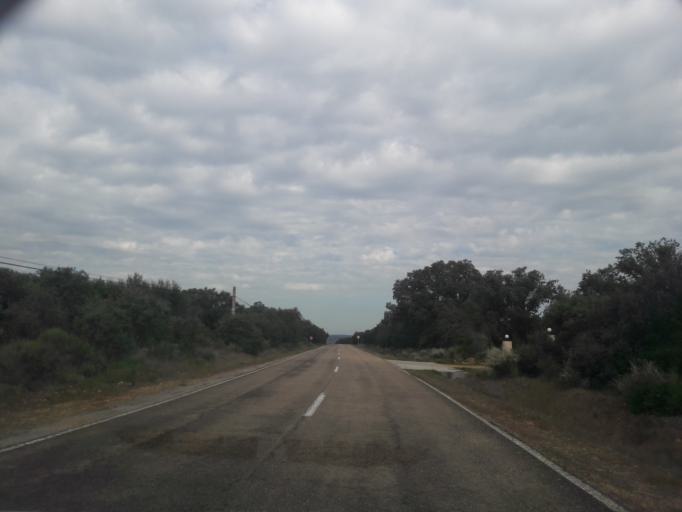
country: ES
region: Castille and Leon
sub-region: Provincia de Salamanca
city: Ciudad Rodrigo
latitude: 40.5738
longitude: -6.5312
